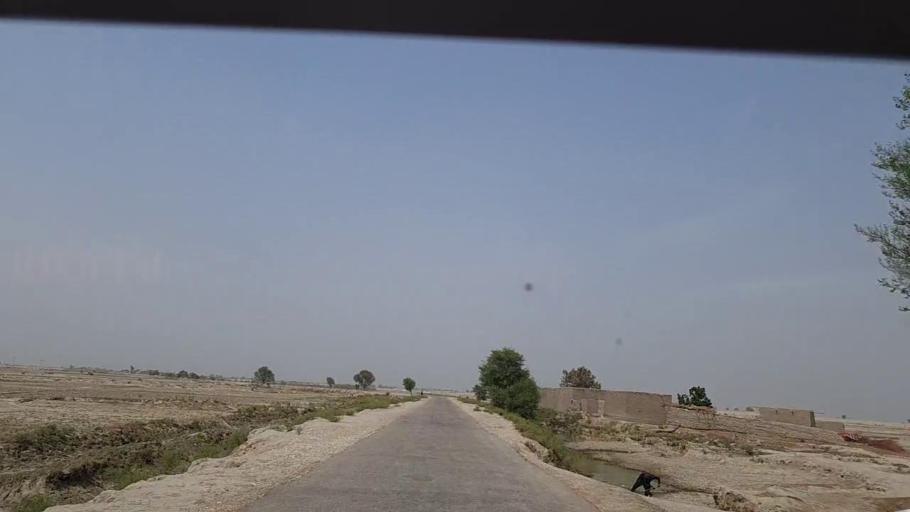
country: PK
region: Sindh
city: Khairpur Nathan Shah
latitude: 27.0544
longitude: 67.6463
